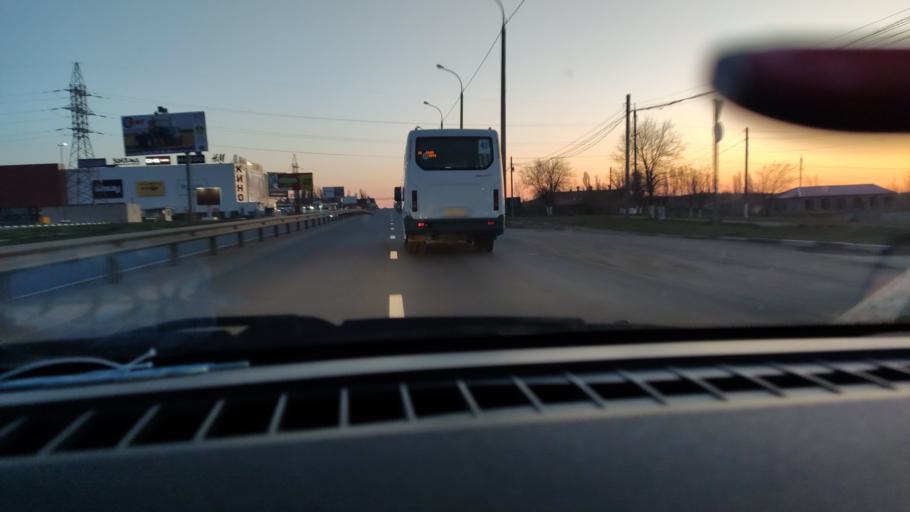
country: RU
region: Saratov
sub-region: Saratovskiy Rayon
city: Saratov
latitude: 51.6211
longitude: 45.9752
